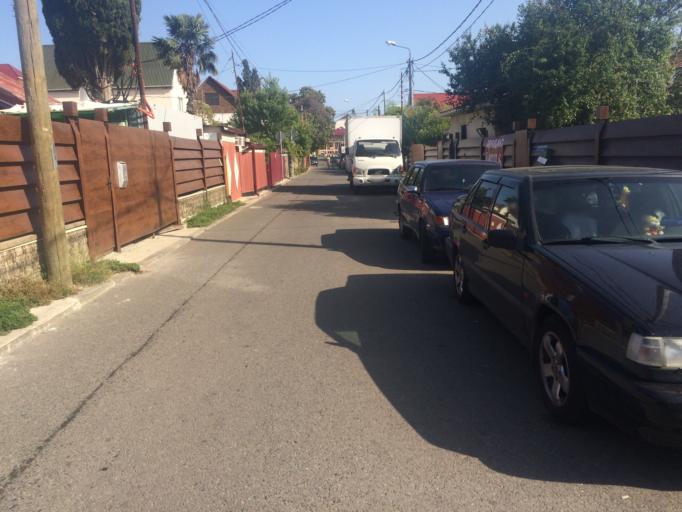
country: RU
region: Krasnodarskiy
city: Adler
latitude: 43.3935
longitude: 39.9849
